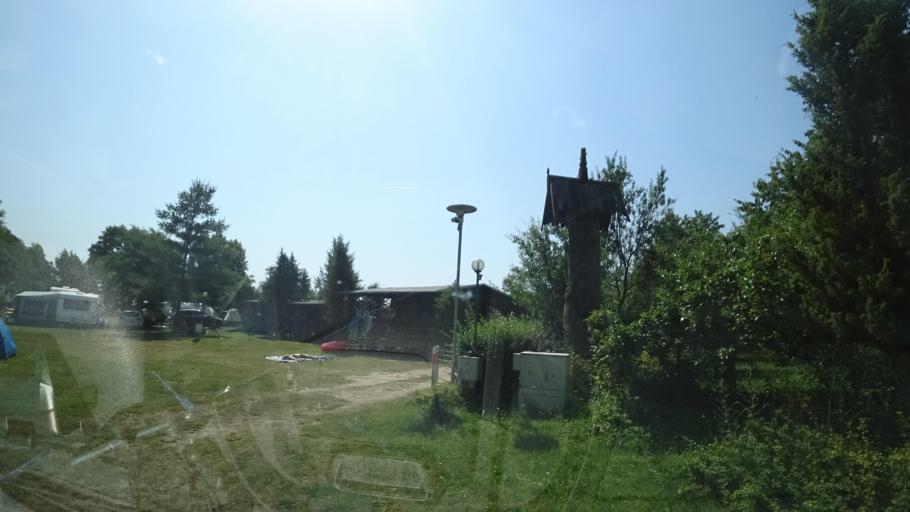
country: PL
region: Pomeranian Voivodeship
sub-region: Powiat chojnicki
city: Brusy
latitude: 53.8703
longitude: 17.5474
